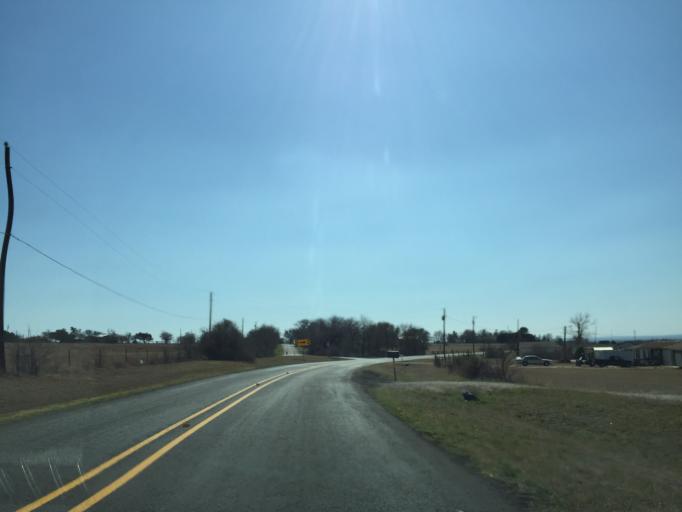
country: US
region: Texas
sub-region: Williamson County
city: Serenada
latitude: 30.7133
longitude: -97.5779
